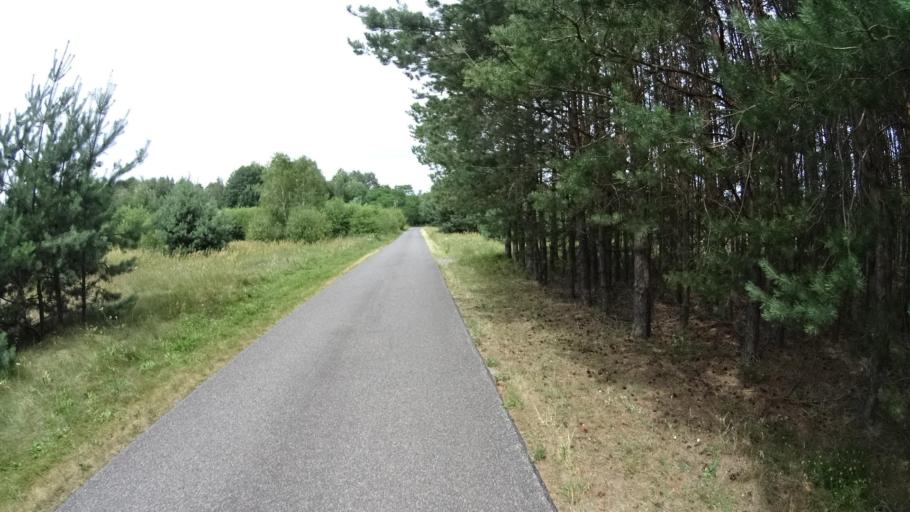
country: PL
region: Masovian Voivodeship
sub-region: Powiat bialobrzeski
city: Bialobrzegi
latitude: 51.6413
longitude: 20.9027
